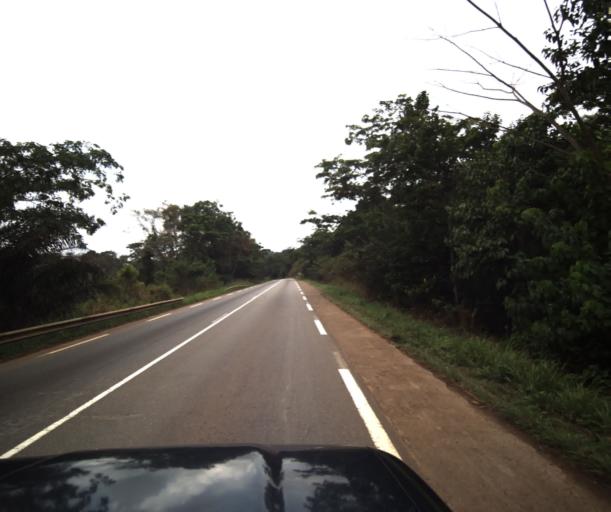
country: CM
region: Centre
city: Eseka
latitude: 3.8300
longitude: 10.9983
